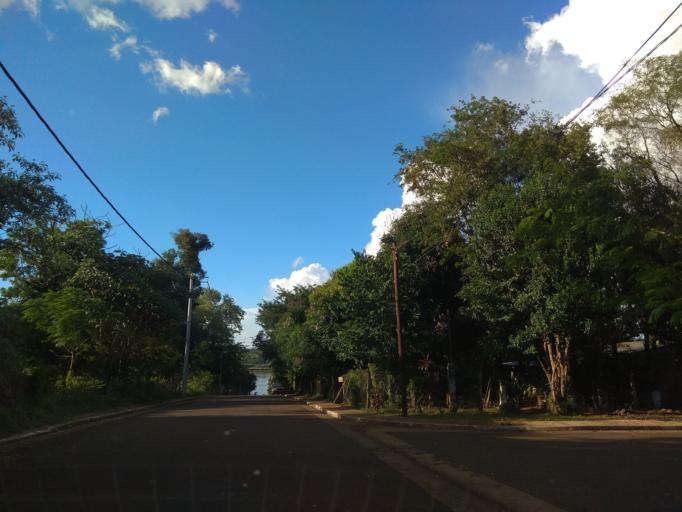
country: AR
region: Misiones
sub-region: Departamento de Candelaria
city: Candelaria
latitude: -27.4511
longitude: -55.7489
